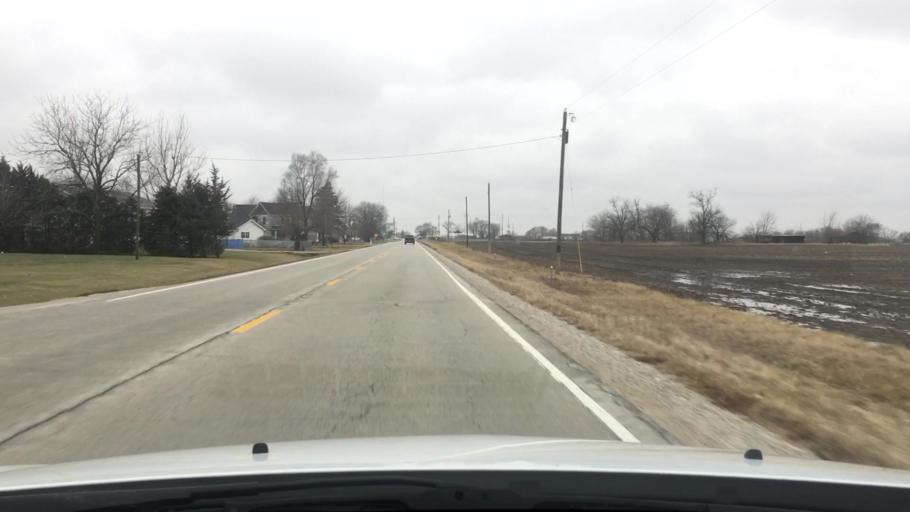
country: US
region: Illinois
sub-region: Iroquois County
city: Clifton
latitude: 40.8850
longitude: -87.9460
